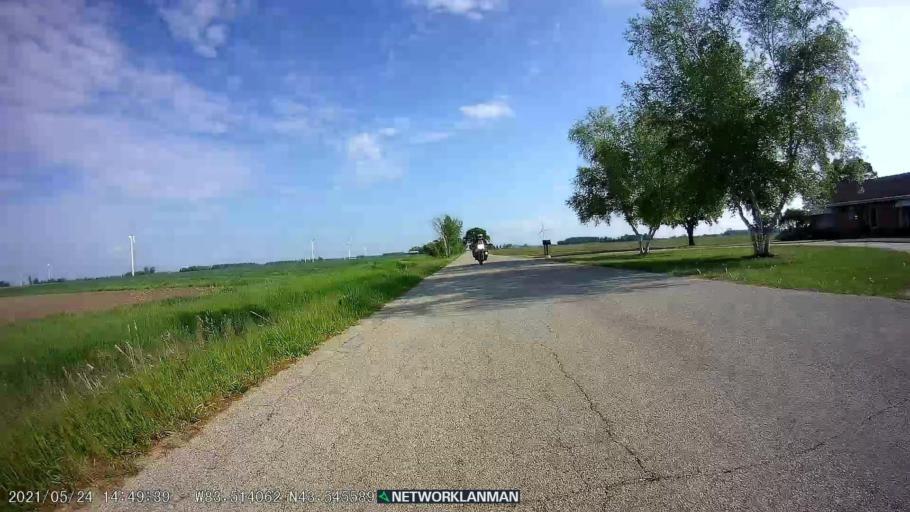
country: US
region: Michigan
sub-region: Tuscola County
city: Caro
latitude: 43.5456
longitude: -83.5141
